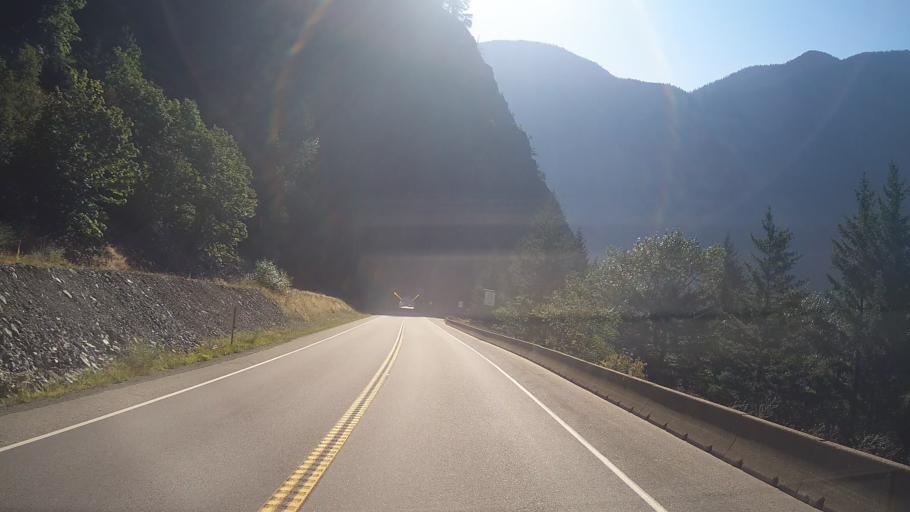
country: CA
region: British Columbia
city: Hope
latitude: 49.5631
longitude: -121.4176
